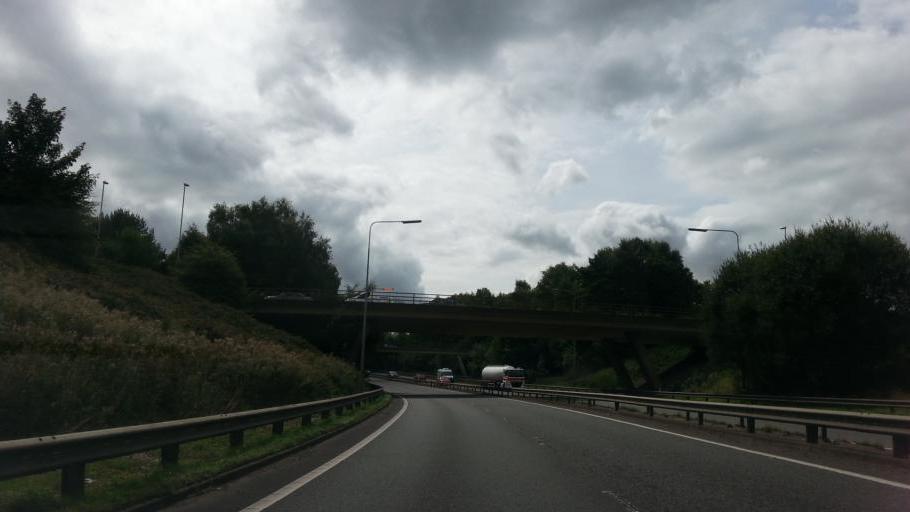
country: GB
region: England
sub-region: Northamptonshire
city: Hardingstone
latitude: 52.2157
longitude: -0.8927
